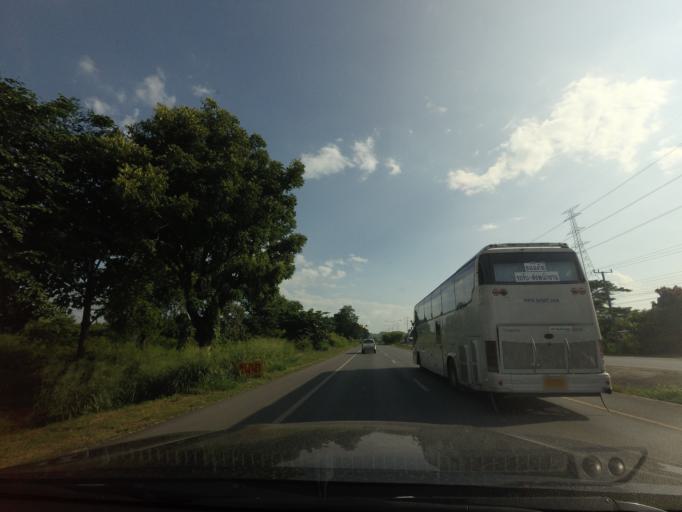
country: TH
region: Lop Buri
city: Phatthana Nikhom
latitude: 14.7883
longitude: 100.9126
